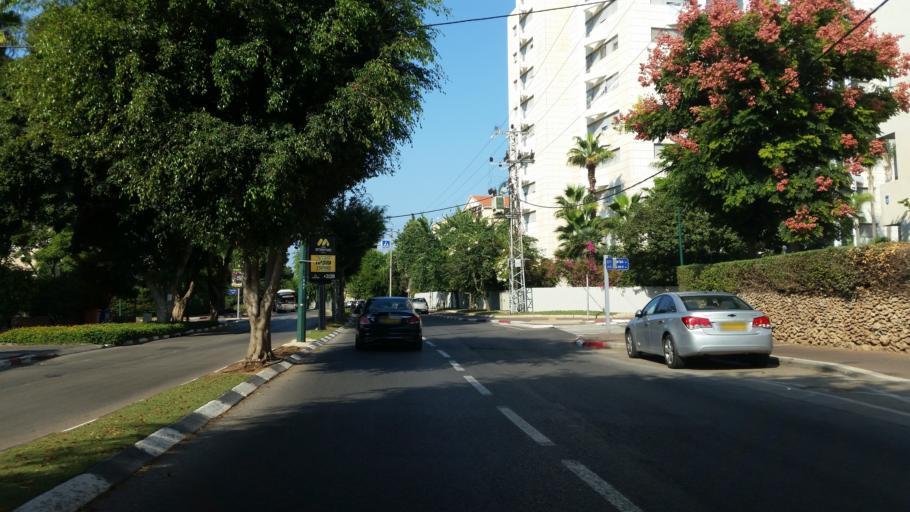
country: IL
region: Tel Aviv
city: Ramat HaSharon
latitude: 32.1613
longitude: 34.8412
